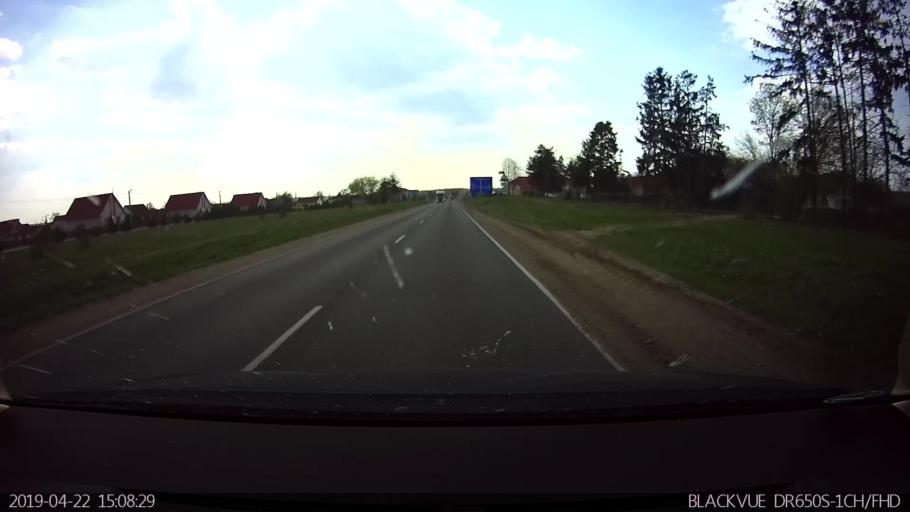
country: BY
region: Brest
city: Kamyanyets
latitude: 52.3269
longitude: 23.7869
